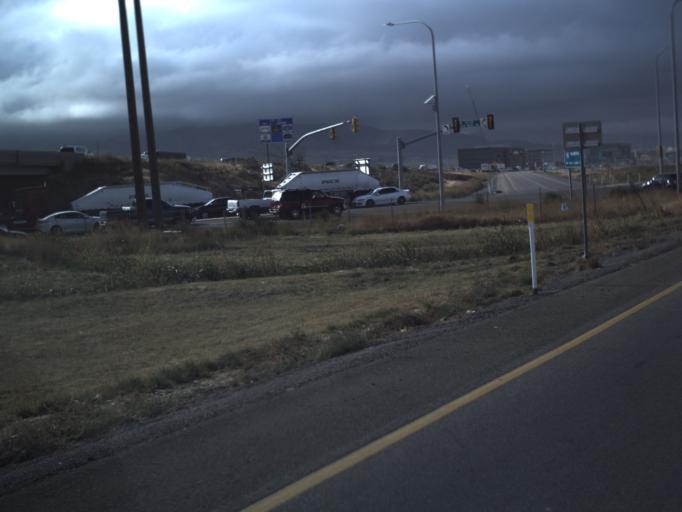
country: US
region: Utah
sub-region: Utah County
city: Lehi
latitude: 40.4138
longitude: -111.8677
